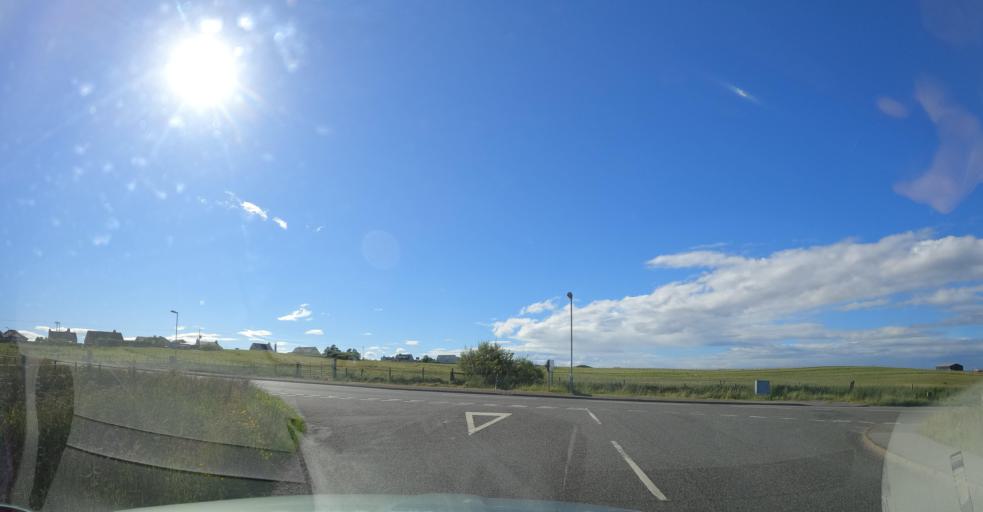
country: GB
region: Scotland
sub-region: Eilean Siar
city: Stornoway
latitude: 58.2162
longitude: -6.2376
